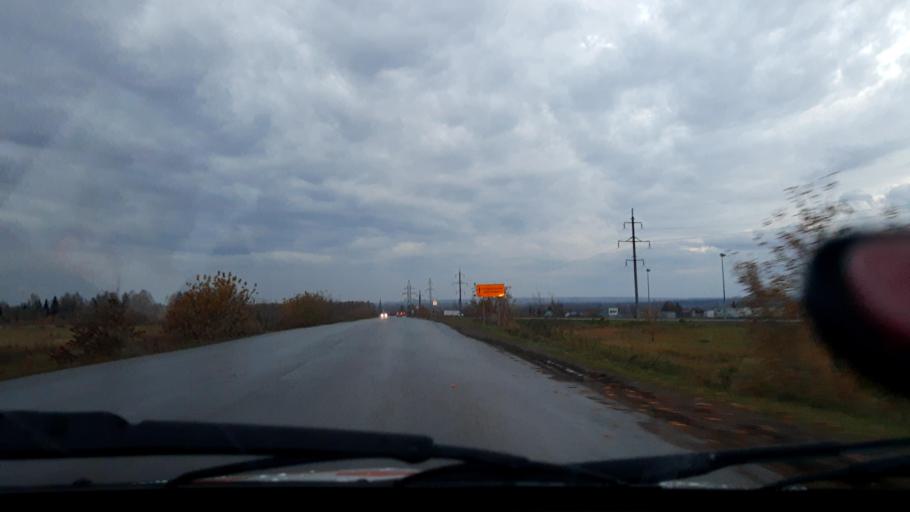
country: RU
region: Bashkortostan
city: Iglino
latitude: 54.7578
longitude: 56.2580
